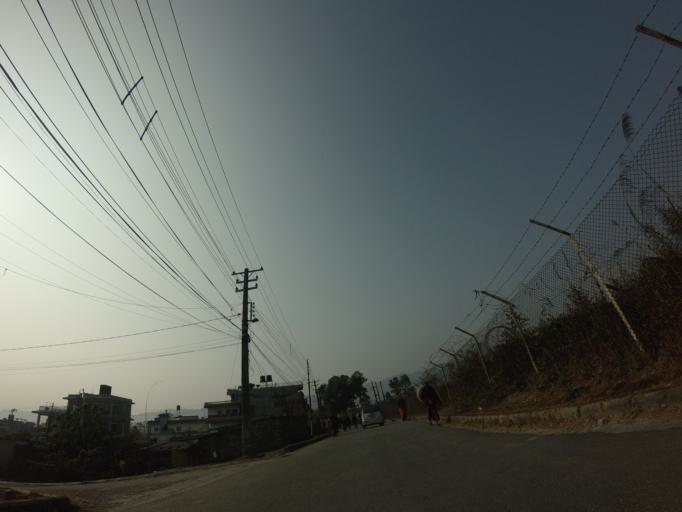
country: NP
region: Western Region
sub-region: Gandaki Zone
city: Pokhara
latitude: 28.1984
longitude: 83.9827
